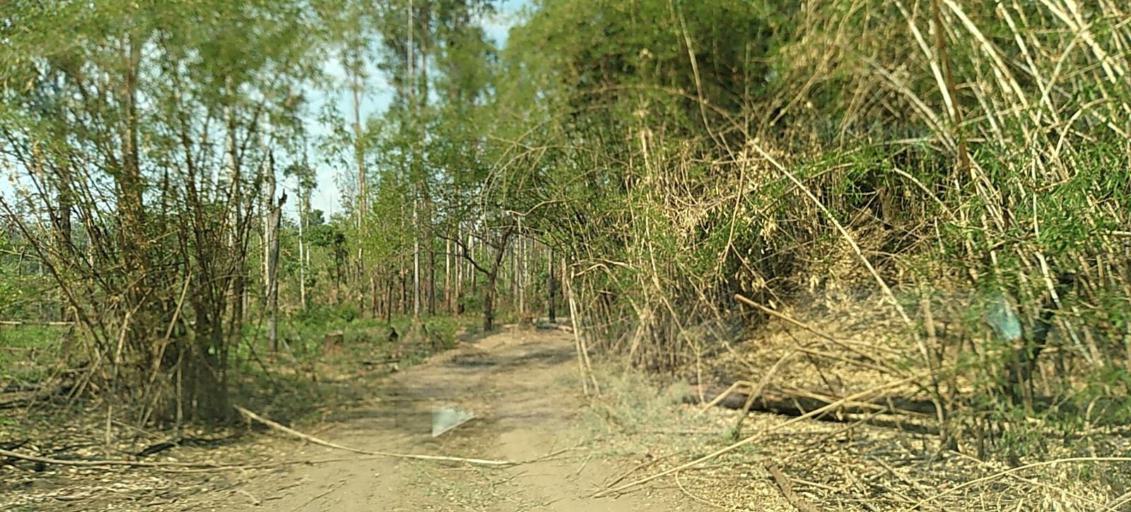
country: ZM
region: Copperbelt
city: Chingola
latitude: -12.7382
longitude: 27.7554
